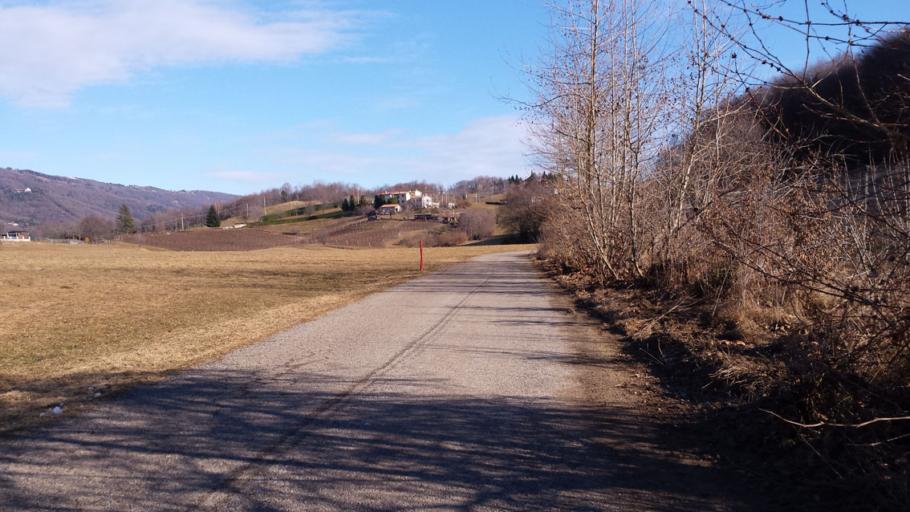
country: IT
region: Veneto
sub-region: Provincia di Treviso
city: Paderno del Grappa
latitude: 45.8361
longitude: 11.8589
